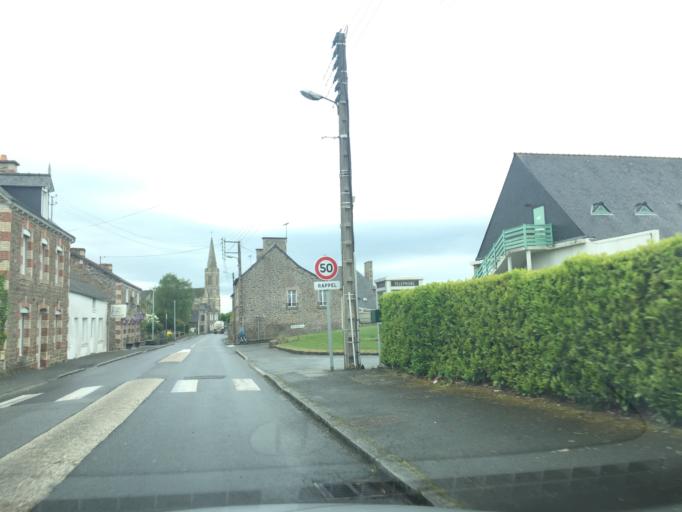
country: FR
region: Brittany
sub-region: Departement des Cotes-d'Armor
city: Crehen
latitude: 48.5476
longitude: -2.2308
